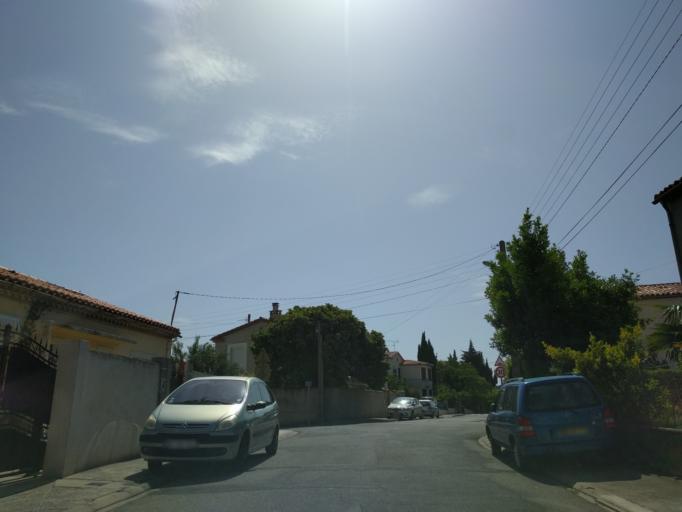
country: FR
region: Languedoc-Roussillon
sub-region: Departement de l'Aude
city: Carcassonne
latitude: 43.2119
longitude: 2.3684
